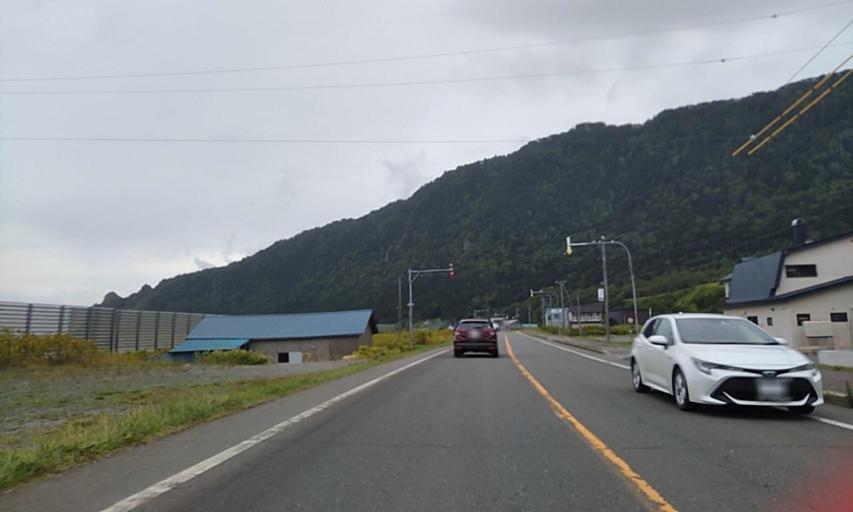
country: JP
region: Hokkaido
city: Nayoro
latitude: 45.0644
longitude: 142.4772
